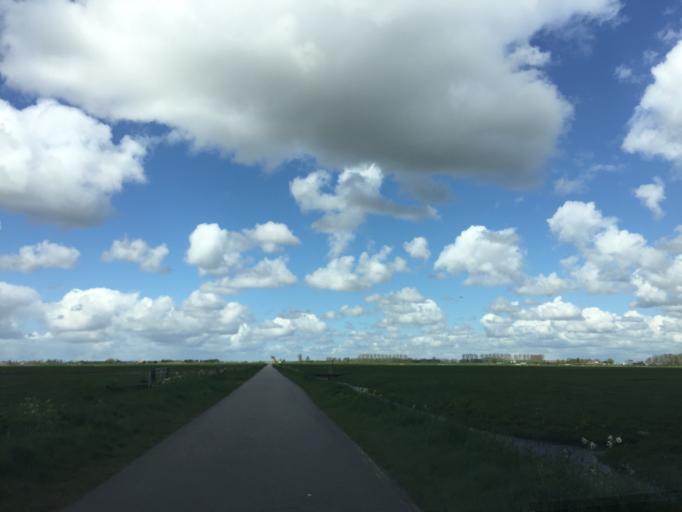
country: NL
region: South Holland
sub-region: Gemeente Kaag en Braassem
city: Oude Wetering
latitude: 52.1991
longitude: 4.6053
